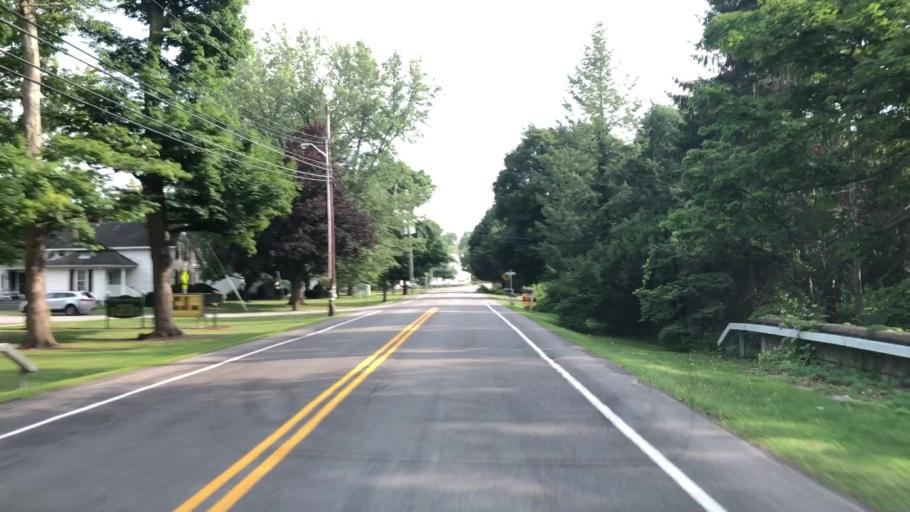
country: US
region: New York
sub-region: Erie County
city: Elma Center
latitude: 42.8513
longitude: -78.6403
